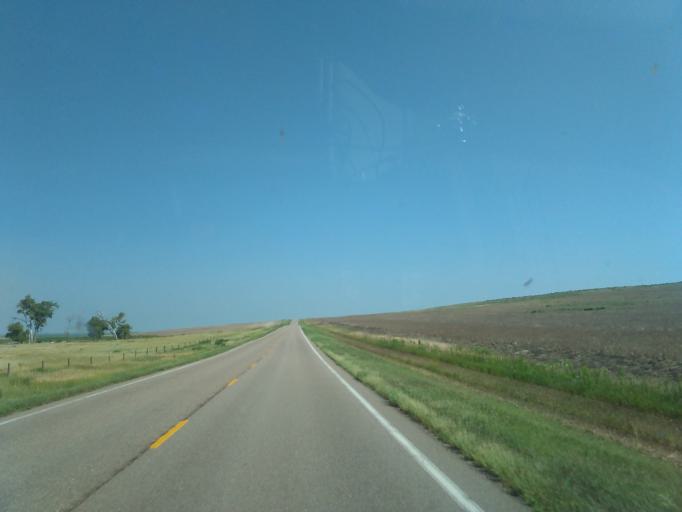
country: US
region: Nebraska
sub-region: Dundy County
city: Benkelman
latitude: 39.9634
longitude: -101.5416
